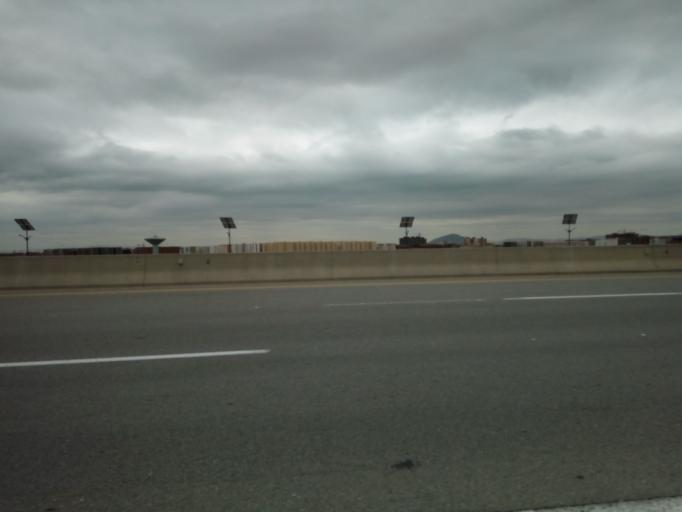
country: DZ
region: Setif
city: El Eulma
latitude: 36.1768
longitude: 5.6777
